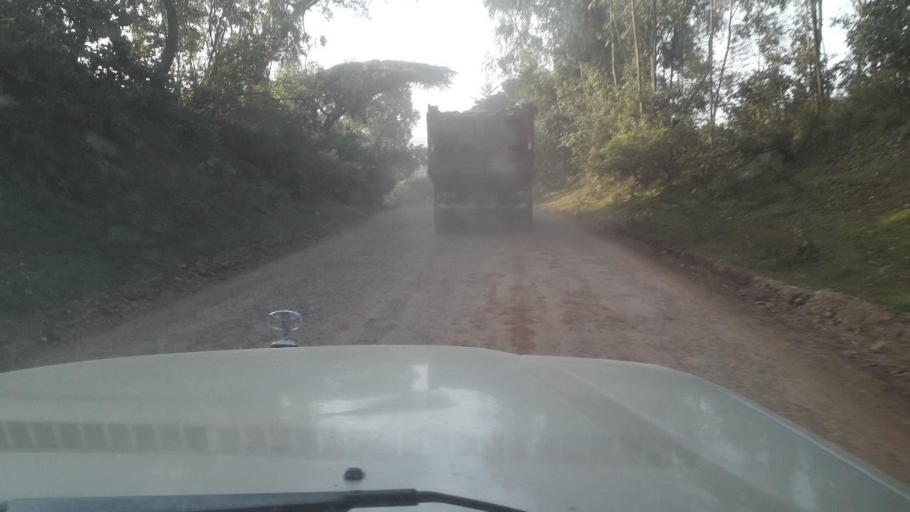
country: ET
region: Oromiya
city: Jima
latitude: 7.6039
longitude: 36.8418
